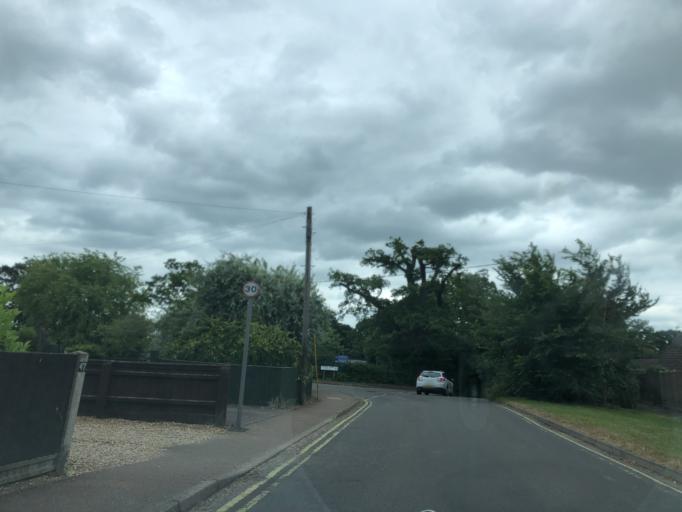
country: GB
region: England
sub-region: Suffolk
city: Thurston
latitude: 52.2503
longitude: 0.8199
